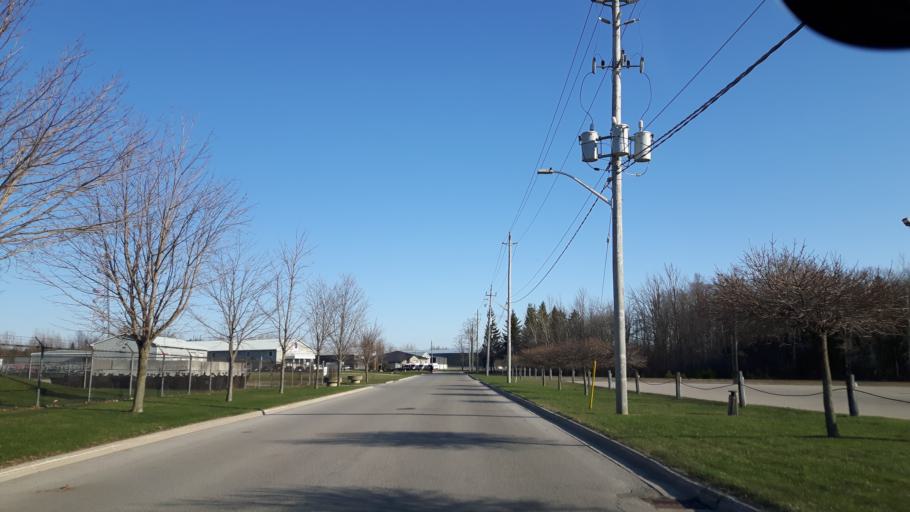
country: CA
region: Ontario
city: Goderich
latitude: 43.7306
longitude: -81.6951
